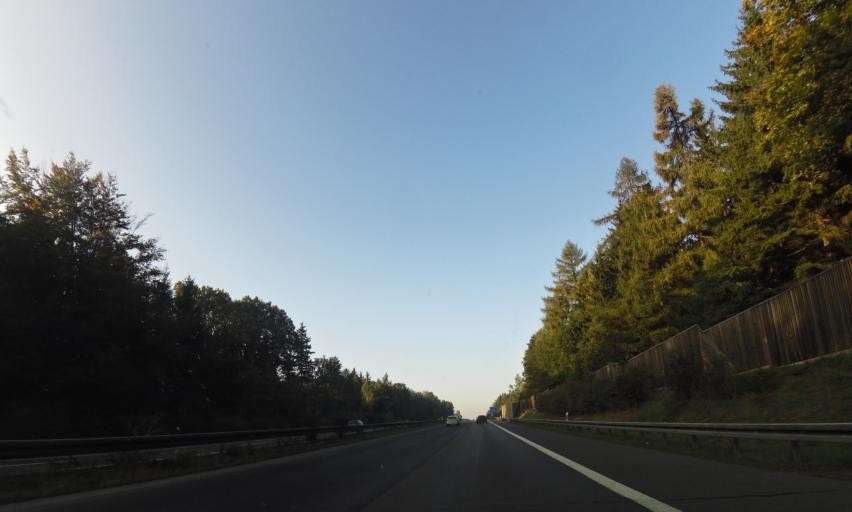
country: DE
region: Saxony
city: Hirschfeld
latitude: 50.6443
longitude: 12.4500
